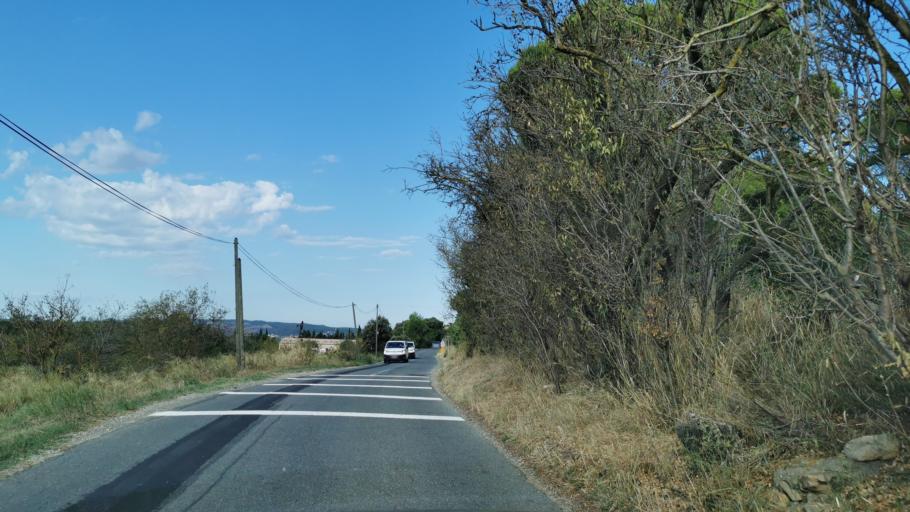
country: FR
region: Languedoc-Roussillon
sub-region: Departement de l'Aude
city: Narbonne
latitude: 43.1422
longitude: 3.0227
